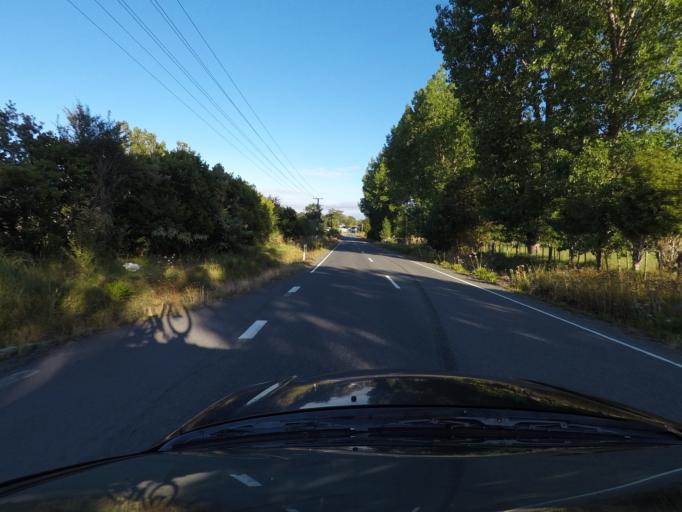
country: NZ
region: Northland
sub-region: Whangarei
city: Whangarei
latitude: -35.6433
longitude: 174.3002
